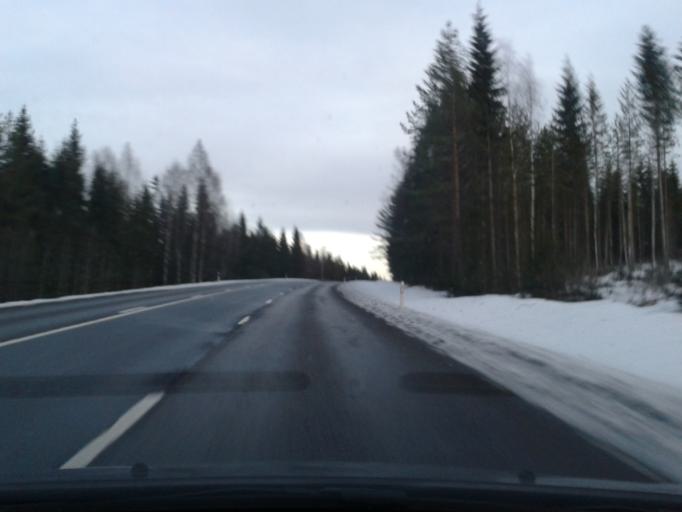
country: SE
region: Vaesternorrland
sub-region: Solleftea Kommun
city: Solleftea
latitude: 63.1372
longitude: 17.4464
